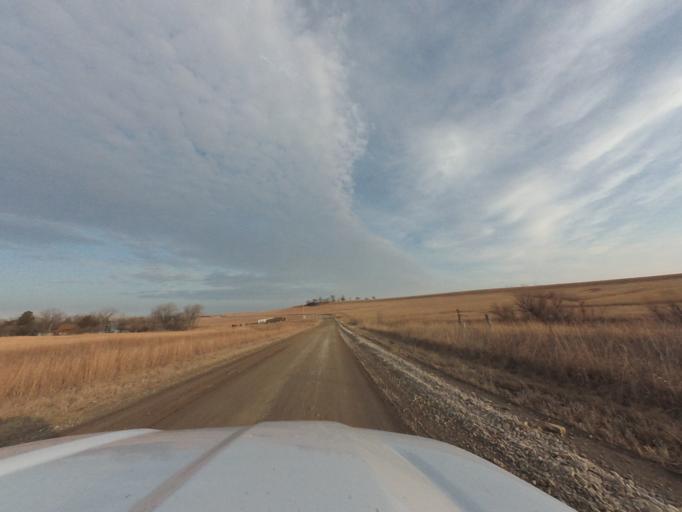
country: US
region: Kansas
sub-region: Morris County
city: Council Grove
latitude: 38.5165
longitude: -96.4096
